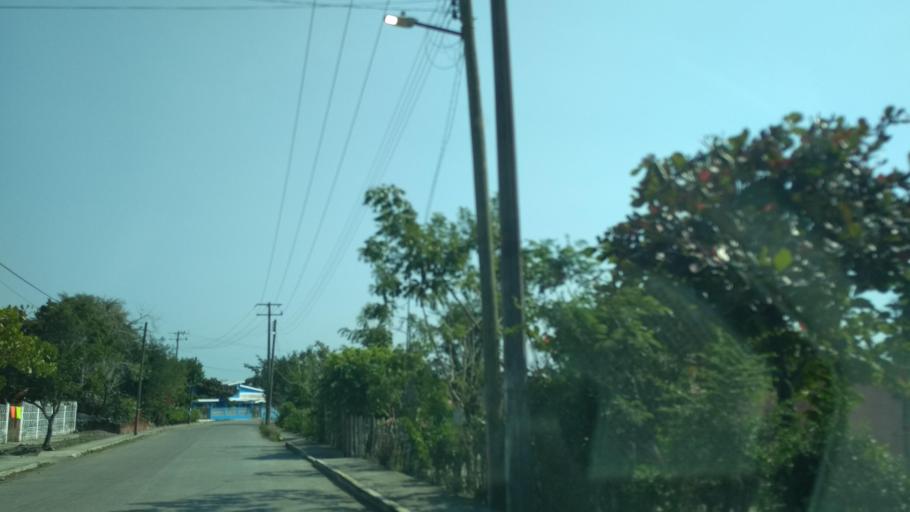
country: MX
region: Veracruz
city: Gutierrez Zamora
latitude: 20.4179
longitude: -97.1881
